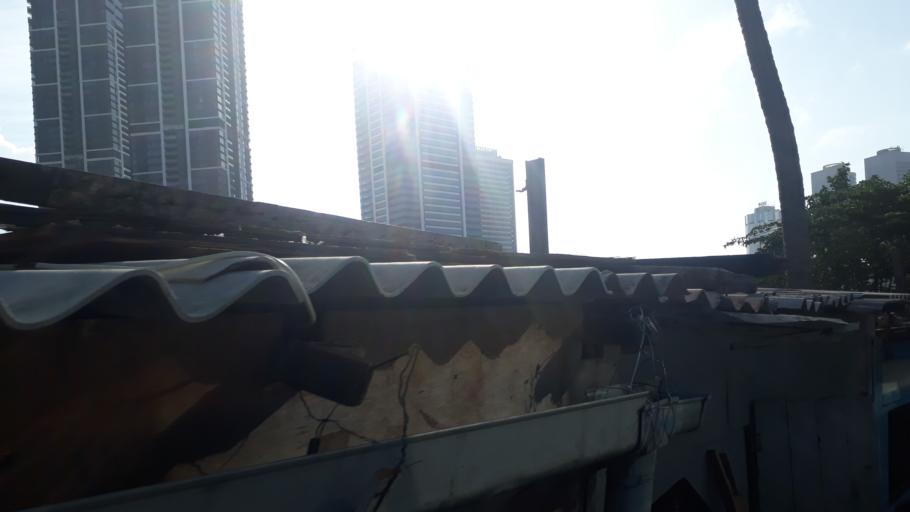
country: LK
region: Western
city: Colombo
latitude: 6.9264
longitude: 79.8486
